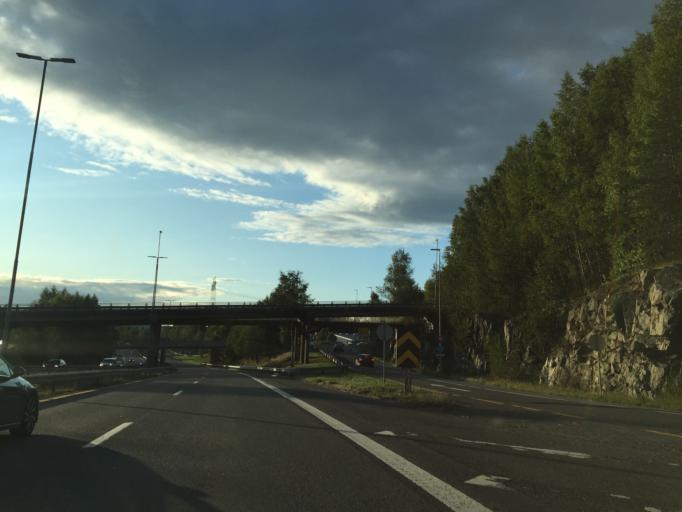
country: NO
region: Akershus
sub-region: Lorenskog
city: Kjenn
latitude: 59.9354
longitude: 10.9388
